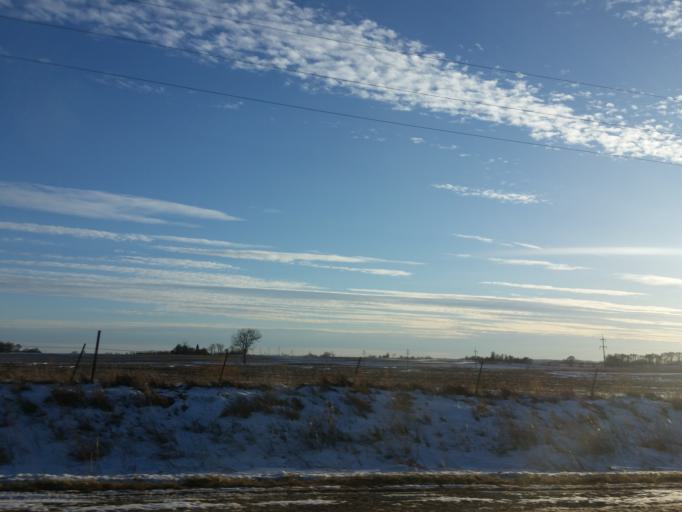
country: US
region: Iowa
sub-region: Butler County
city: Allison
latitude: 42.7450
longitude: -92.8771
